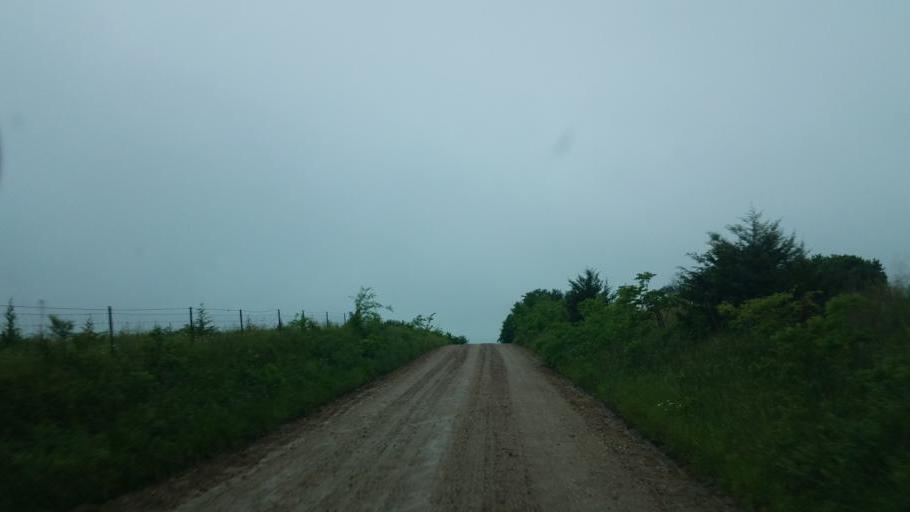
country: US
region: Missouri
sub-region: Moniteau County
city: California
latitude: 38.7454
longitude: -92.6057
